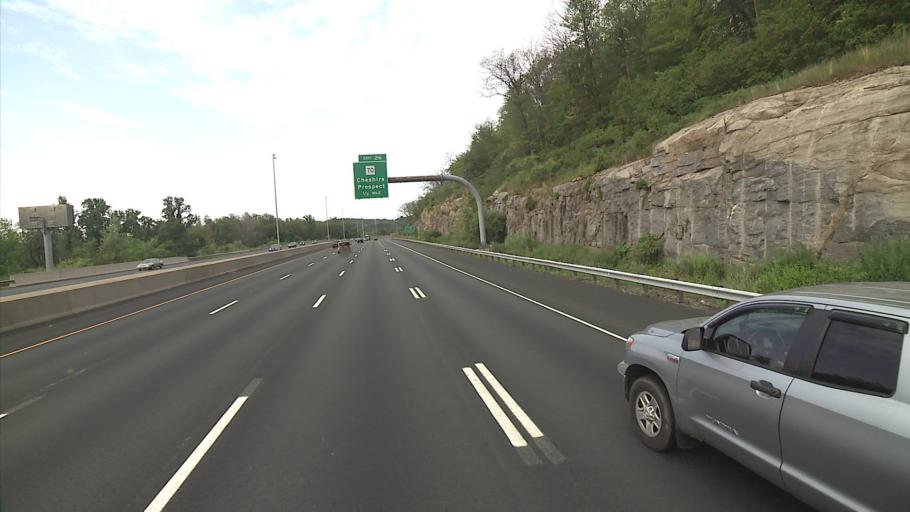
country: US
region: Connecticut
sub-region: New Haven County
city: Prospect
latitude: 41.5455
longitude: -72.9415
